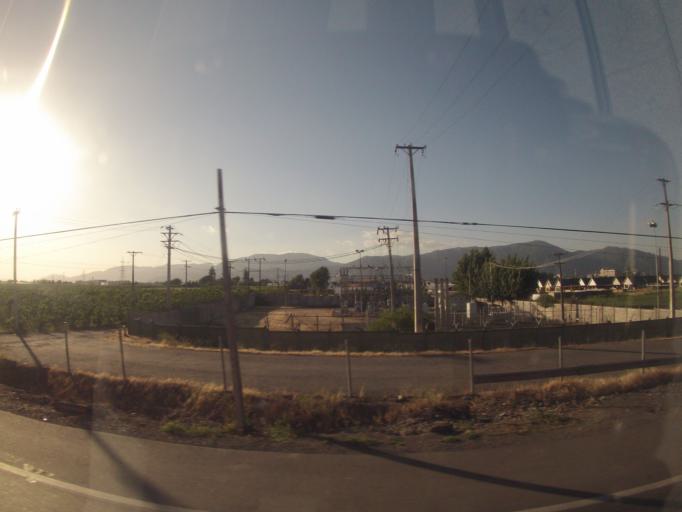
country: CL
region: O'Higgins
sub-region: Provincia de Colchagua
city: Chimbarongo
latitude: -34.6010
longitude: -70.9787
